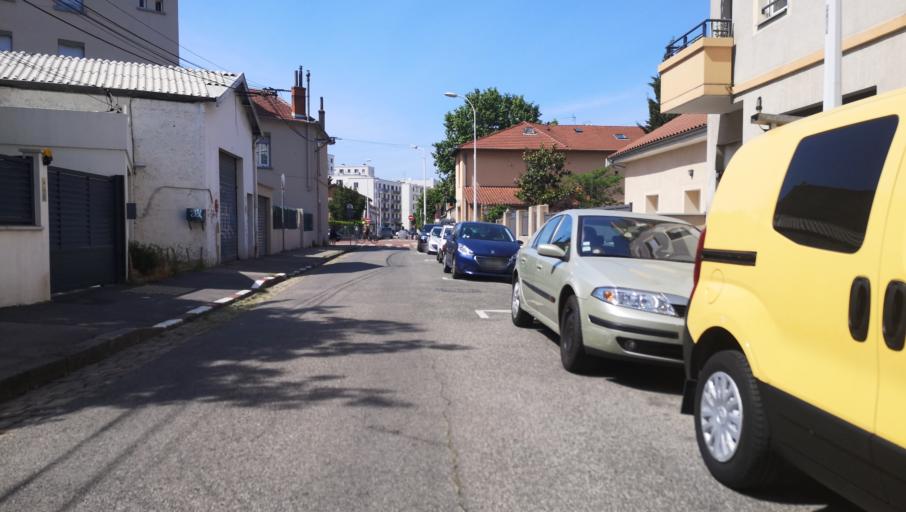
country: FR
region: Rhone-Alpes
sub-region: Departement du Rhone
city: Villeurbanne
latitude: 45.7382
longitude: 4.8786
